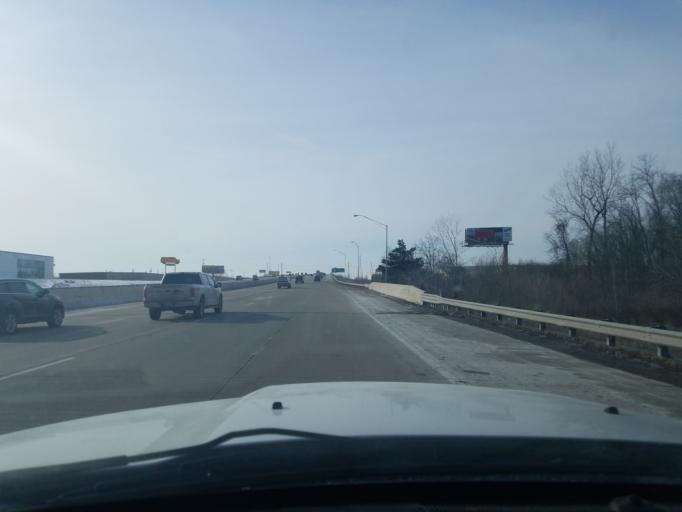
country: US
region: Indiana
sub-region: Allen County
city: Fort Wayne
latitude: 41.1293
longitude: -85.1656
